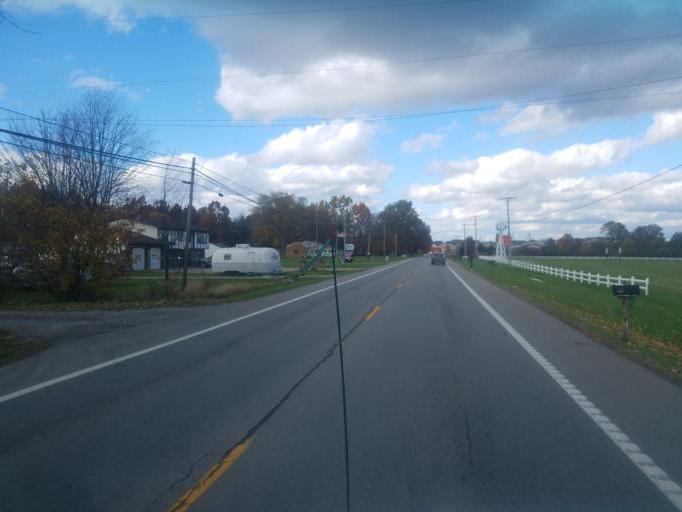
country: US
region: Ohio
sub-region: Wayne County
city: Orrville
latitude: 40.8011
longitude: -81.7653
